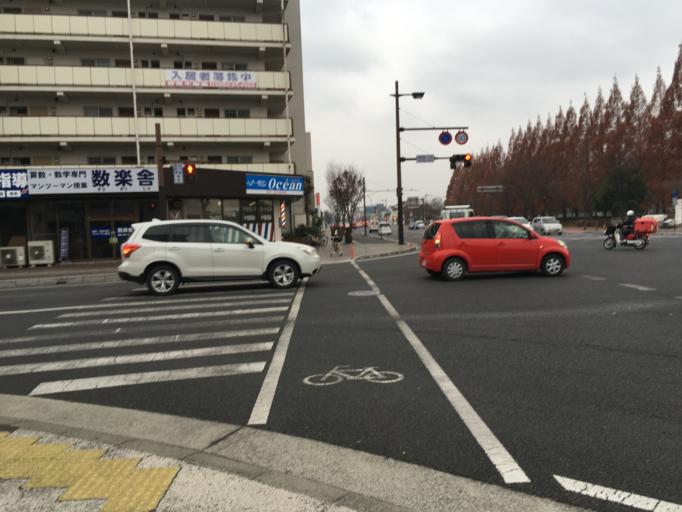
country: JP
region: Saga Prefecture
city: Saga-shi
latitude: 33.2616
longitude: 130.2934
